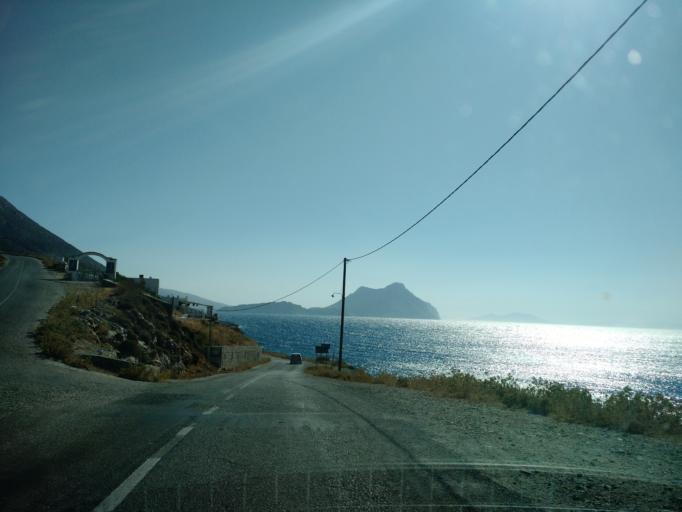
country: GR
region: South Aegean
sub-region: Nomos Kykladon
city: Amorgos
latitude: 36.8980
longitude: 25.9724
